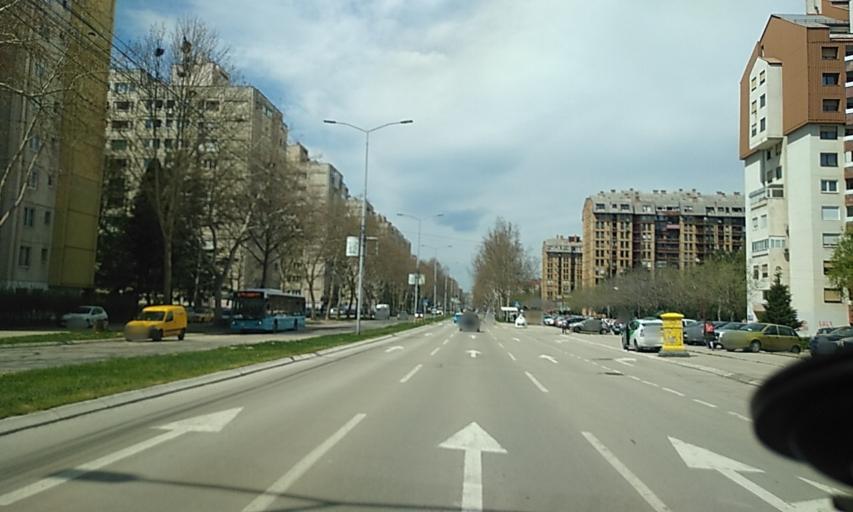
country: RS
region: Central Serbia
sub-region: Nisavski Okrug
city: Nis
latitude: 43.3172
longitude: 21.9239
